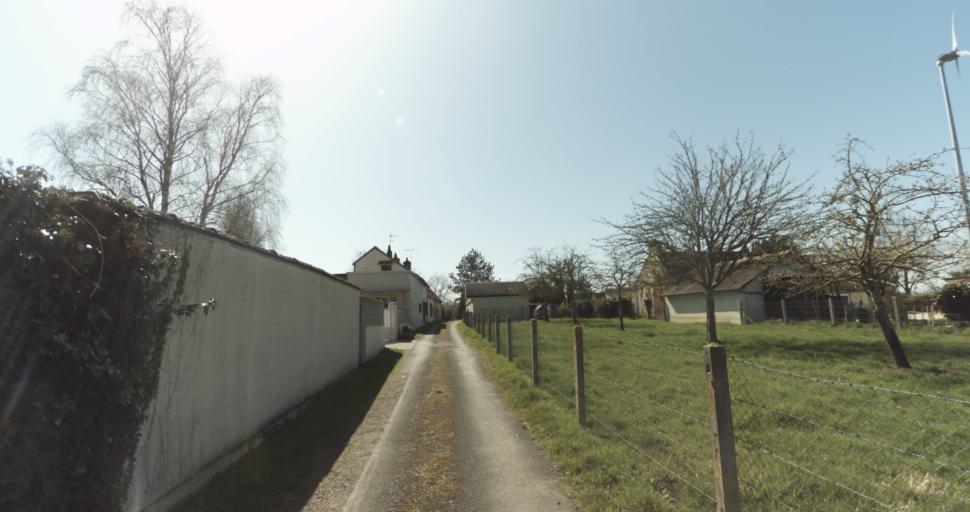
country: FR
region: Lower Normandy
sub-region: Departement du Calvados
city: Saint-Pierre-sur-Dives
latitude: 49.0202
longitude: -0.0104
